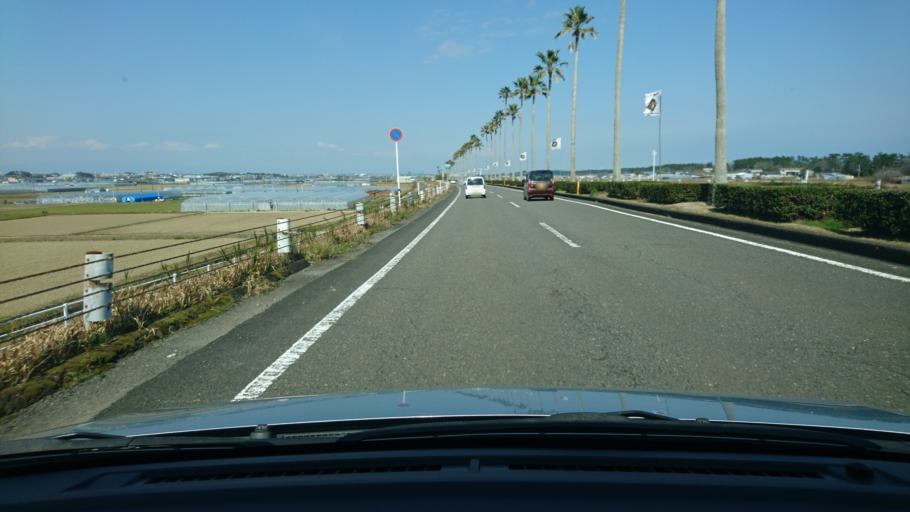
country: JP
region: Miyazaki
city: Miyazaki-shi
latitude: 31.8385
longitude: 131.4448
